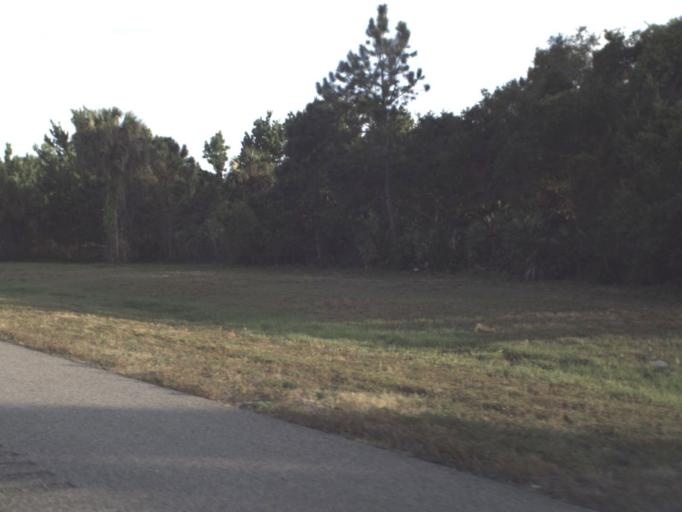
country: US
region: Florida
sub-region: Brevard County
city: Port Saint John
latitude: 28.4840
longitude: -80.8248
